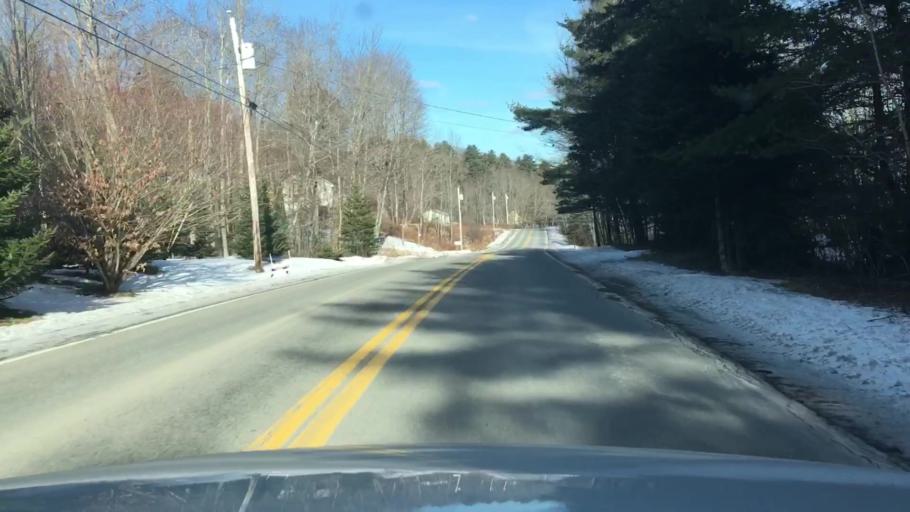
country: US
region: Maine
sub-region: Hancock County
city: Dedham
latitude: 44.6400
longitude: -68.6985
